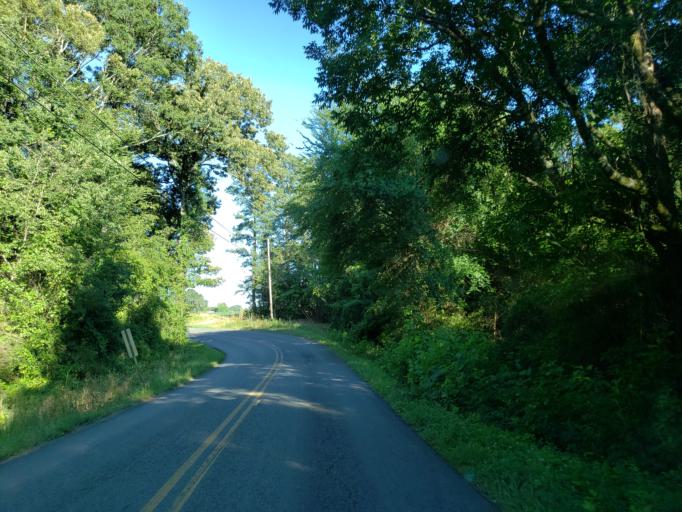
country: US
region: Georgia
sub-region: Bartow County
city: Euharlee
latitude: 34.1258
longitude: -84.9874
